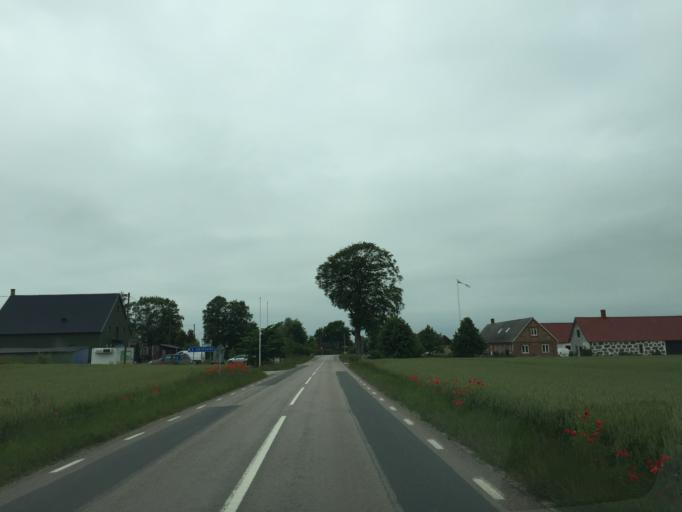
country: SE
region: Skane
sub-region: Ystads Kommun
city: Kopingebro
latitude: 55.4280
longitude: 14.1006
